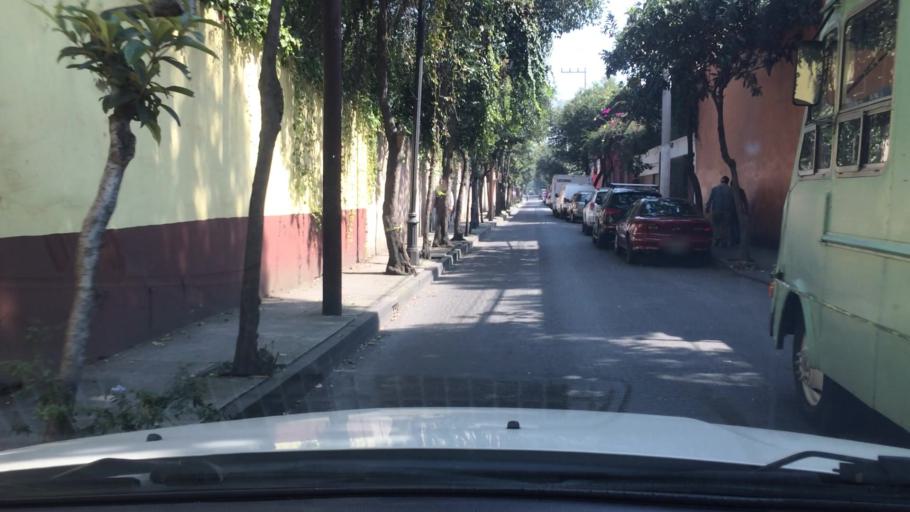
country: MX
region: Mexico City
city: Tlalpan
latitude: 19.2909
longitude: -99.1676
